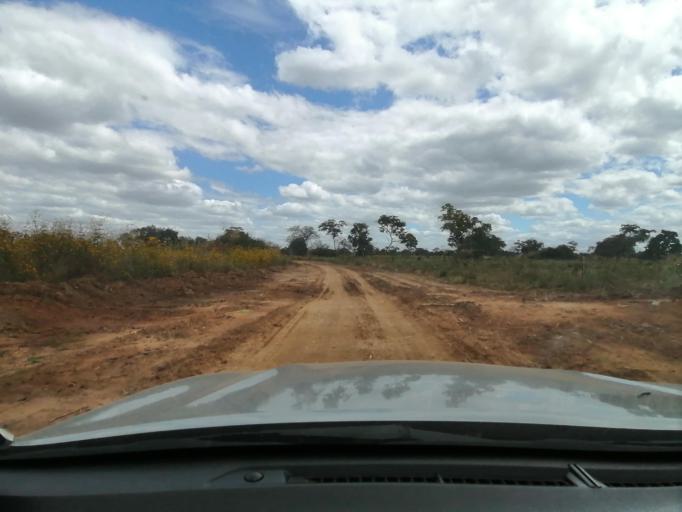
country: ZM
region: Central
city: Mumbwa
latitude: -14.5812
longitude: 27.2236
